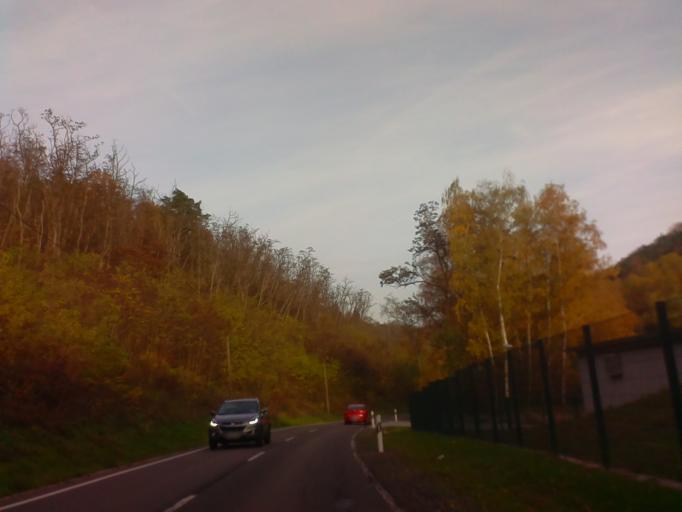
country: DE
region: Rheinland-Pfalz
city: Tiefenthal
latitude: 49.5347
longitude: 8.1158
